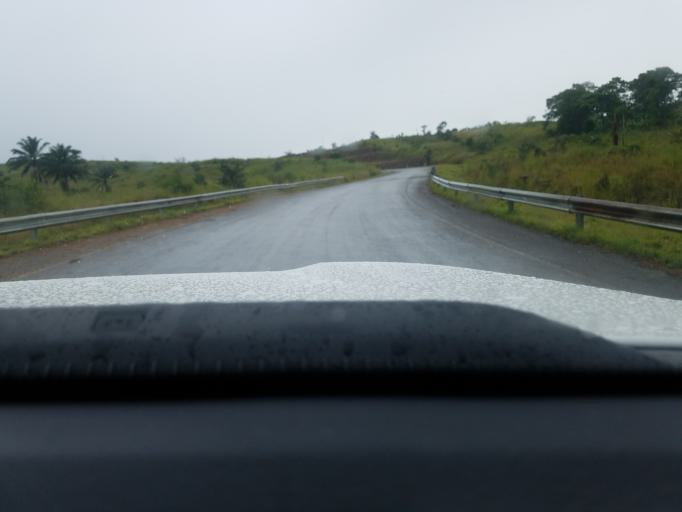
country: TZ
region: Kigoma
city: Mwandiga
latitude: -4.6688
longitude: 29.7244
